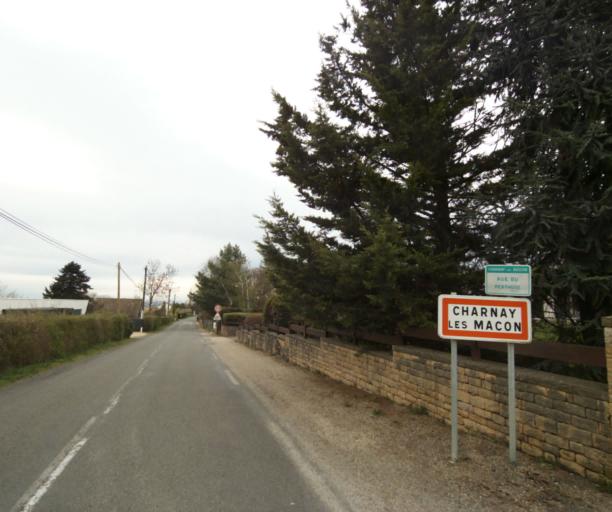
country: FR
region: Bourgogne
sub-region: Departement de Saone-et-Loire
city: Charnay-les-Macon
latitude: 46.3240
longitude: 4.7869
